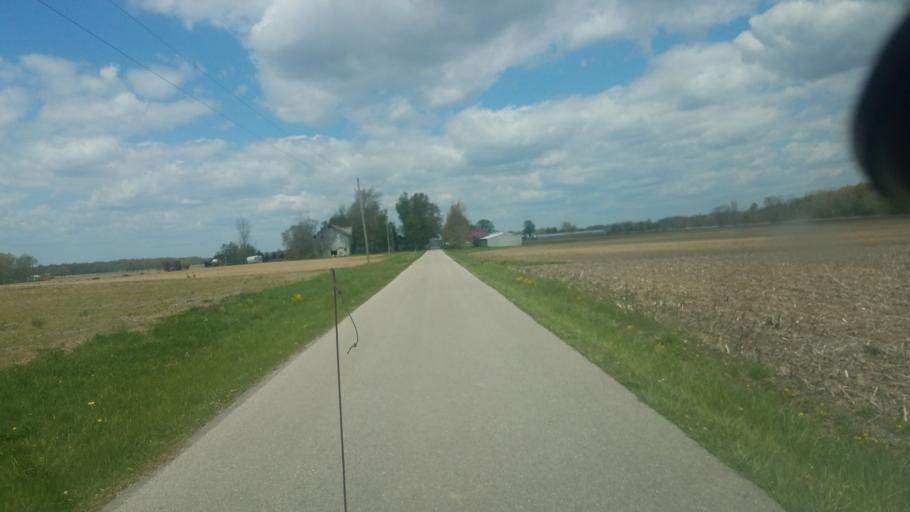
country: US
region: Ohio
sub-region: Crawford County
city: Galion
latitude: 40.7225
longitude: -82.8650
